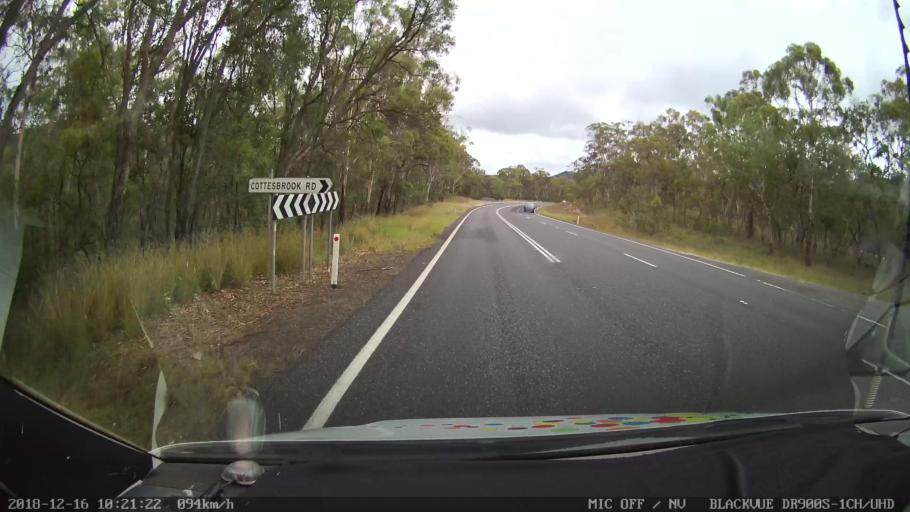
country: AU
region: New South Wales
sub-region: Tenterfield Municipality
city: Carrolls Creek
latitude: -29.2078
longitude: 152.0128
